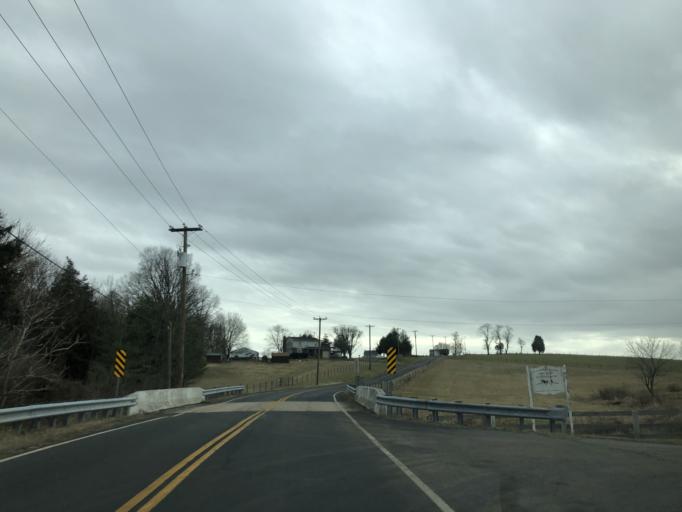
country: US
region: Maryland
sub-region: Cecil County
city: North East
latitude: 39.6819
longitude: -75.9515
